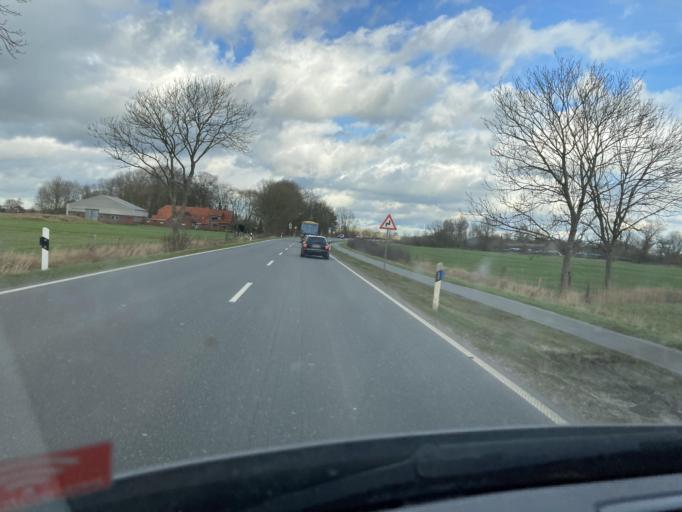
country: DE
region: Lower Saxony
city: Zetel
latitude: 53.4690
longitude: 7.9542
